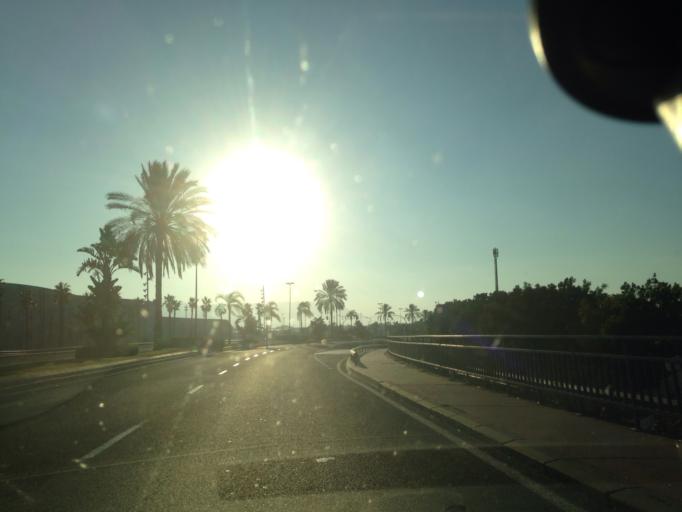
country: ES
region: Andalusia
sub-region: Provincia de Malaga
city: Malaga
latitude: 36.7082
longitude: -4.4587
